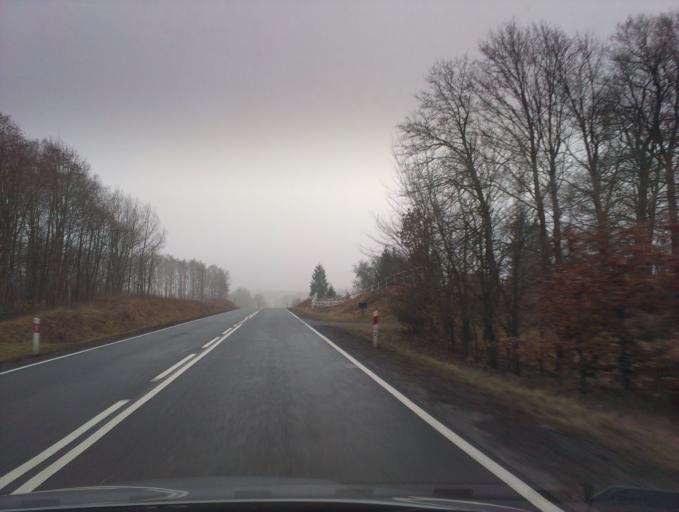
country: PL
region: West Pomeranian Voivodeship
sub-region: Powiat koszalinski
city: Bobolice
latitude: 53.8903
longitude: 16.6131
